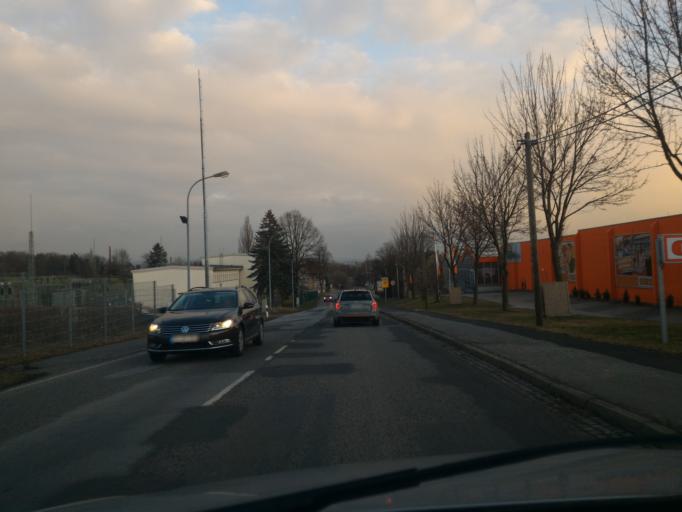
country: DE
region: Saxony
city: Mittelherwigsdorf
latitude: 50.9048
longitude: 14.7726
